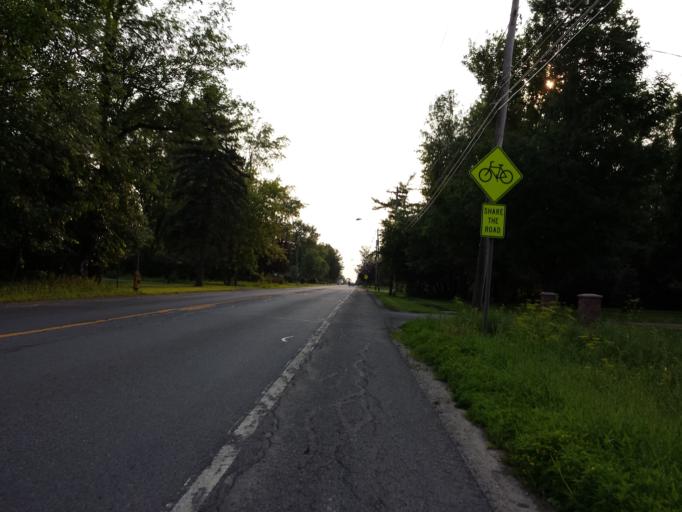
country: US
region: New York
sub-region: St. Lawrence County
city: Potsdam
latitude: 44.6700
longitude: -74.9696
